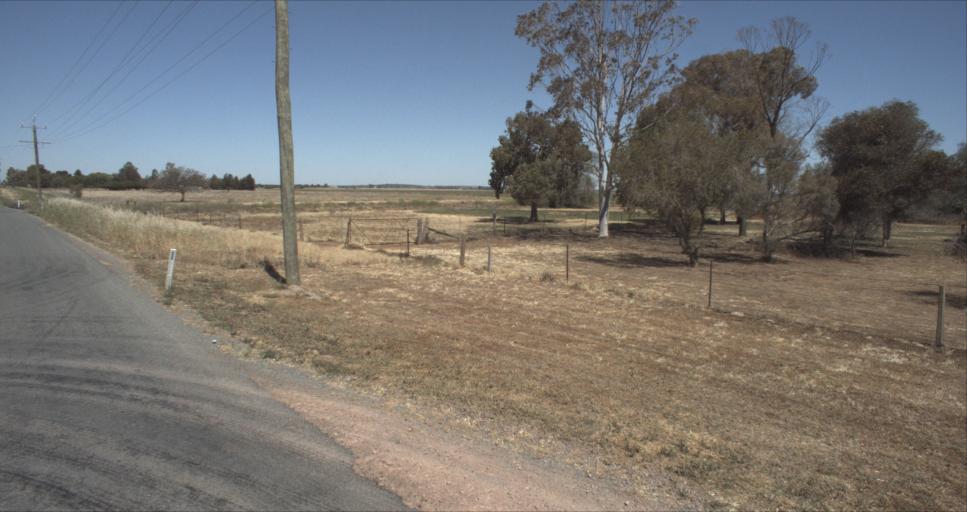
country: AU
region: New South Wales
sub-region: Leeton
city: Leeton
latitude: -34.5174
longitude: 146.4350
